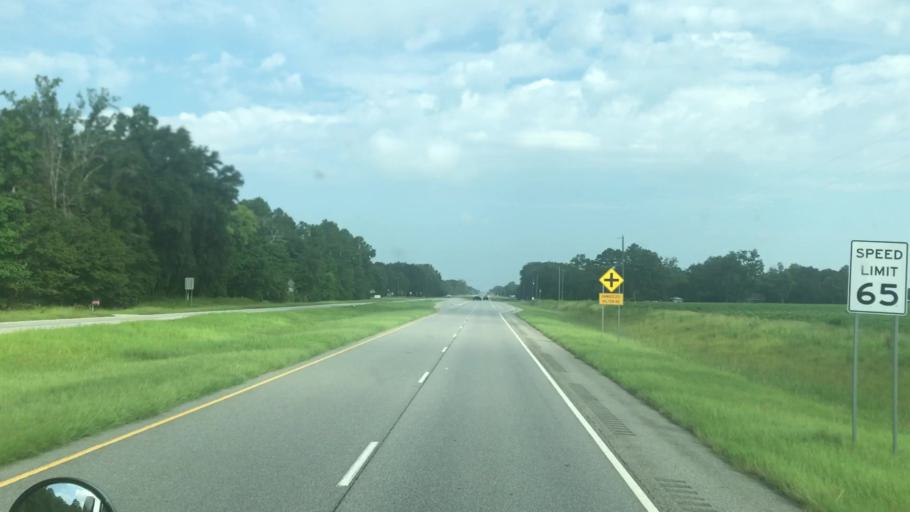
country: US
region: Georgia
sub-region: Early County
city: Blakely
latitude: 31.2777
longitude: -84.8342
